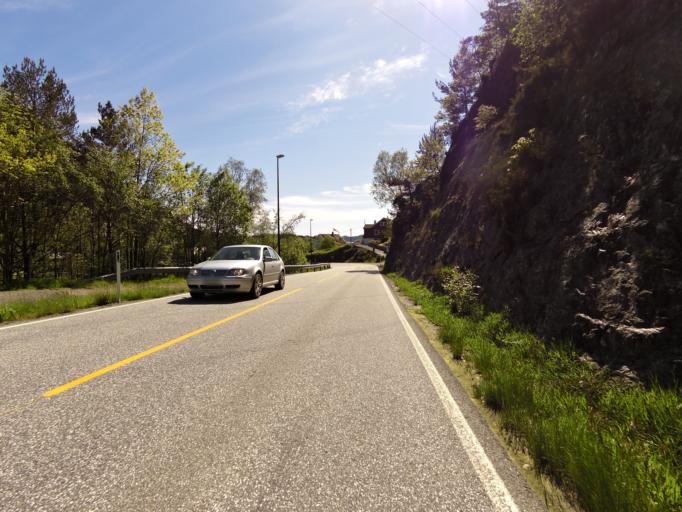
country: NO
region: Hordaland
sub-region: Stord
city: Sagvag
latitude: 59.7928
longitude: 5.3730
